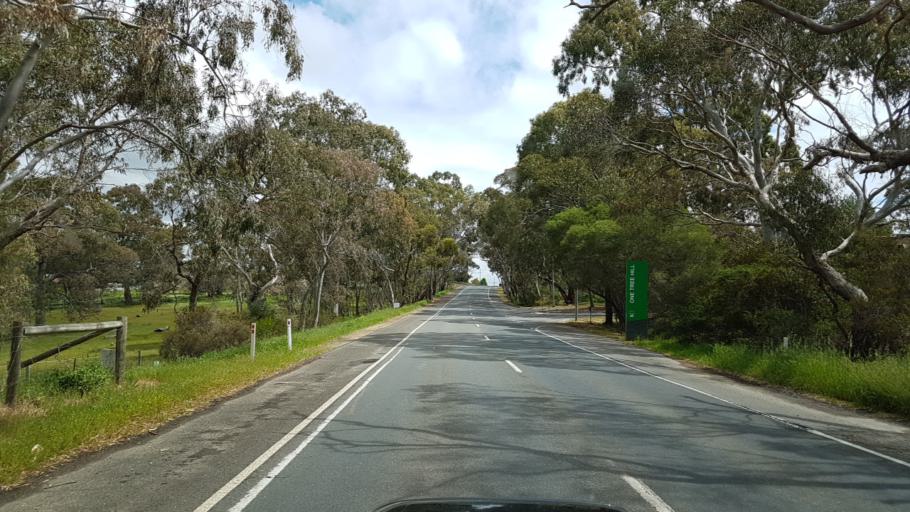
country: AU
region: South Australia
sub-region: Playford
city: One Tree Hill
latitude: -34.7185
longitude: 138.7721
